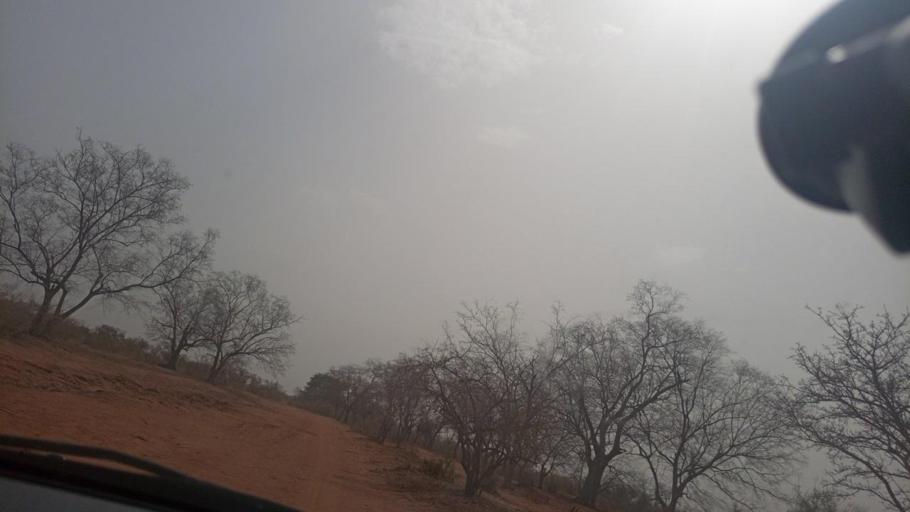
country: BF
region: Boucle du Mouhoun
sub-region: Province des Banwa
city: Salanso
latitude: 12.1874
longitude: -4.2172
